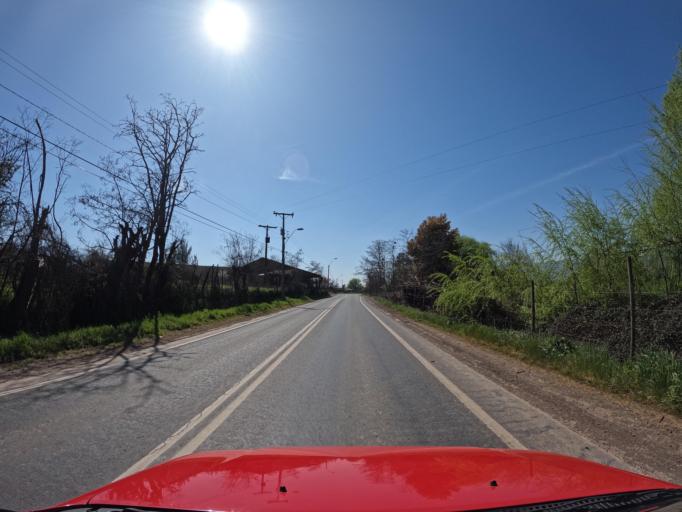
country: CL
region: Maule
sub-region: Provincia de Curico
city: Rauco
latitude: -35.0472
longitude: -71.4660
